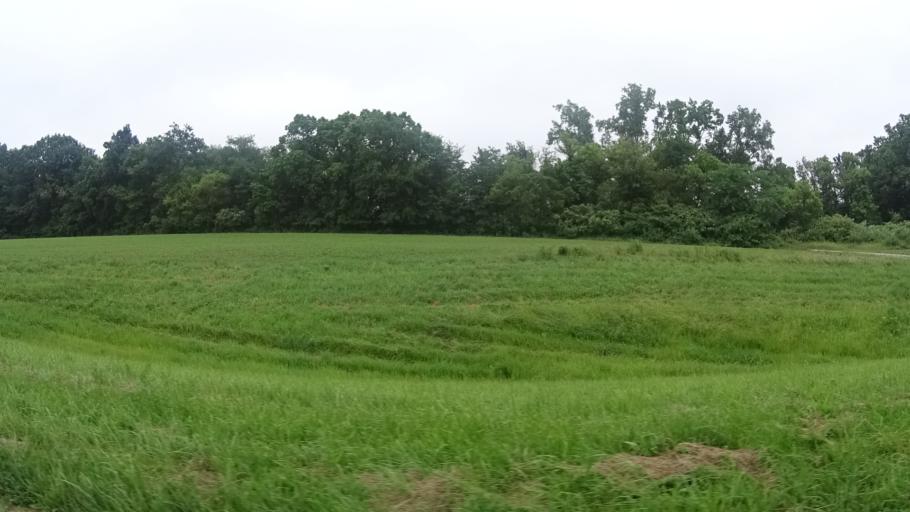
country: US
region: Ohio
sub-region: Erie County
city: Milan
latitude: 41.3355
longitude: -82.5693
